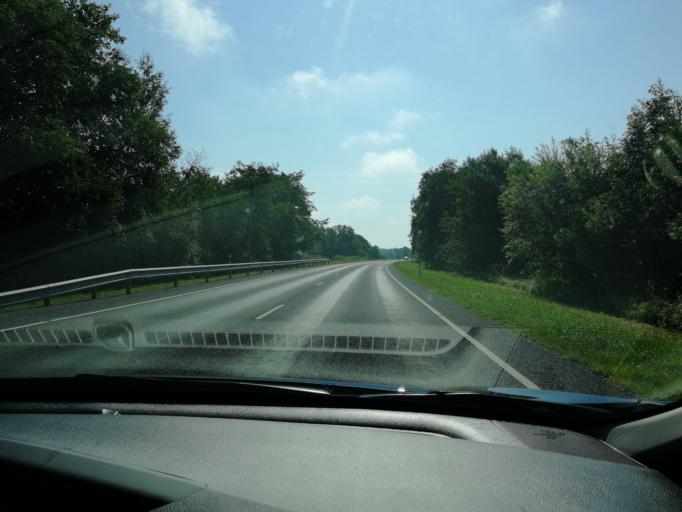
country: EE
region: Paernumaa
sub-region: Saarde vald
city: Kilingi-Nomme
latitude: 58.1909
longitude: 24.7746
